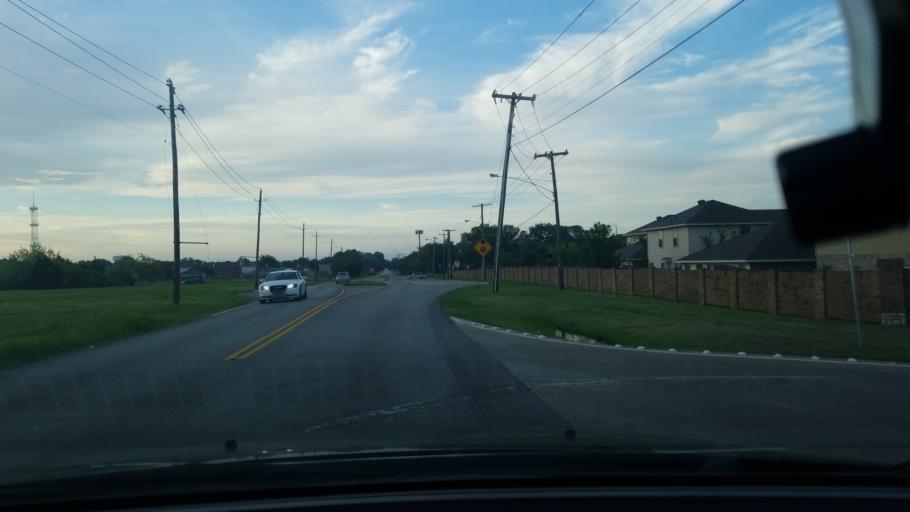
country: US
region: Texas
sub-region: Dallas County
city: Balch Springs
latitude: 32.7673
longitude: -96.6490
